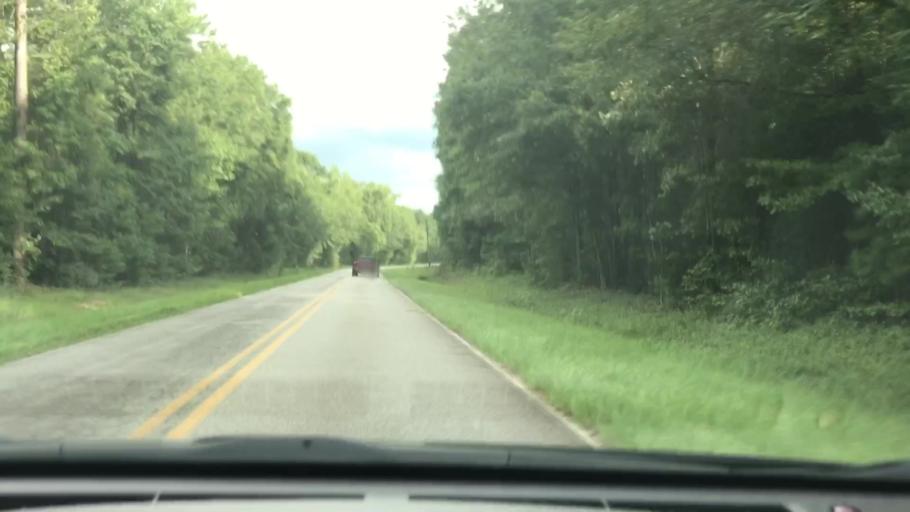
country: US
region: Georgia
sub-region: Jefferson County
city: Wadley
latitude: 32.8218
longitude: -82.3782
